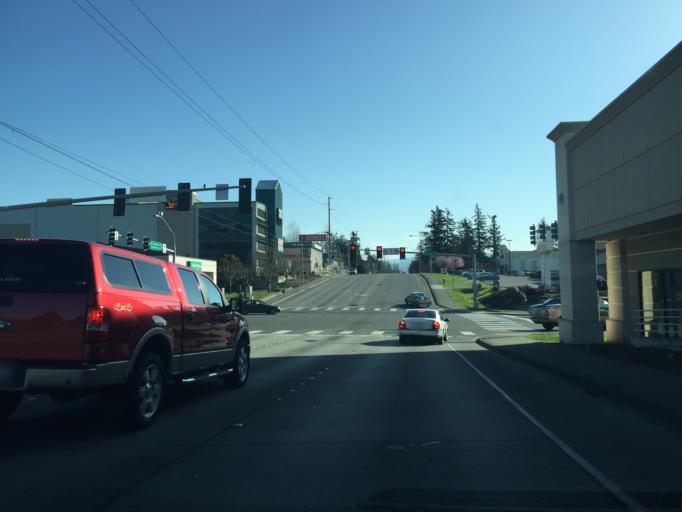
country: US
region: Washington
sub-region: Whatcom County
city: Bellingham
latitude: 48.7897
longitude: -122.4867
